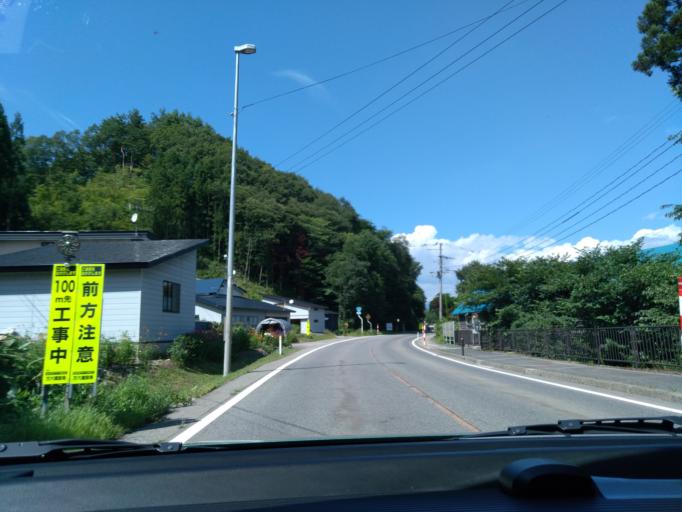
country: JP
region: Akita
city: Kakunodatemachi
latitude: 39.6831
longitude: 140.7070
